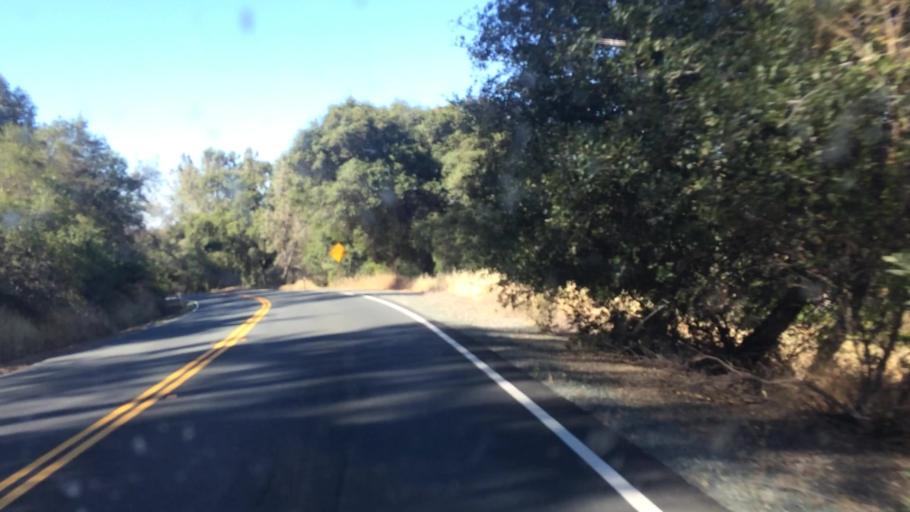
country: US
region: California
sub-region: El Dorado County
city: Deer Park
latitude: 38.6292
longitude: -120.8528
